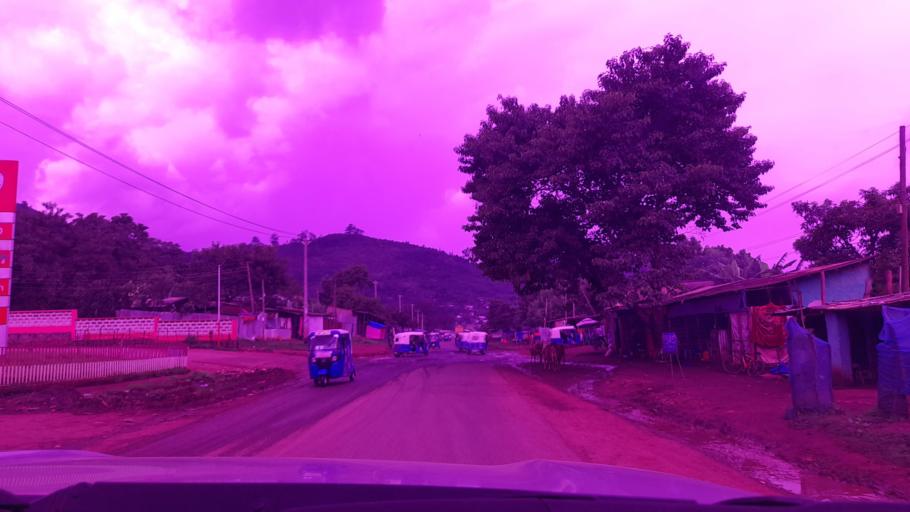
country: ET
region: Oromiya
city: Jima
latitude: 7.6694
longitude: 36.8631
